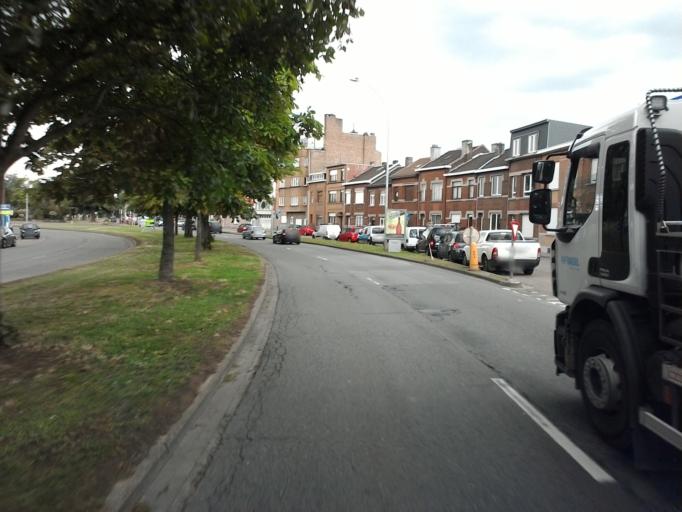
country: BE
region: Wallonia
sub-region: Province de Liege
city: Liege
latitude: 50.6214
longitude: 5.5944
